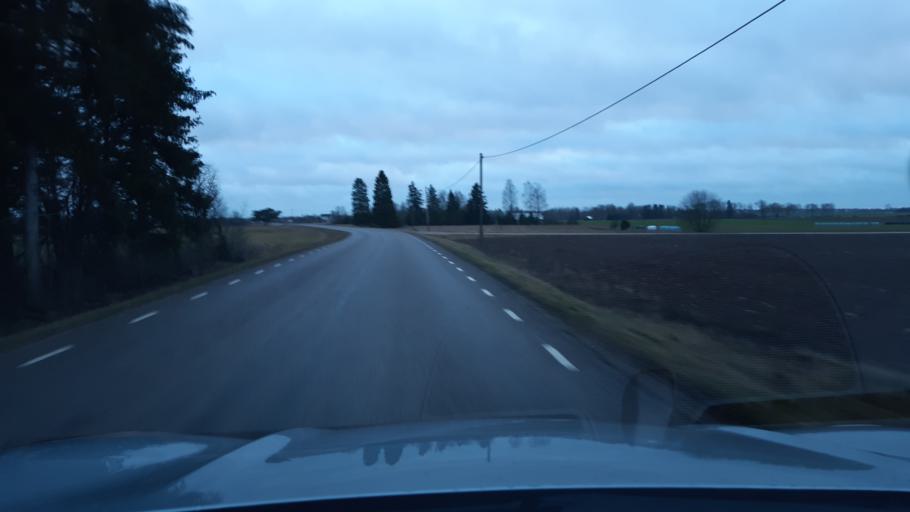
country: EE
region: Raplamaa
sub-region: Kohila vald
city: Kohila
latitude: 59.0685
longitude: 24.6834
